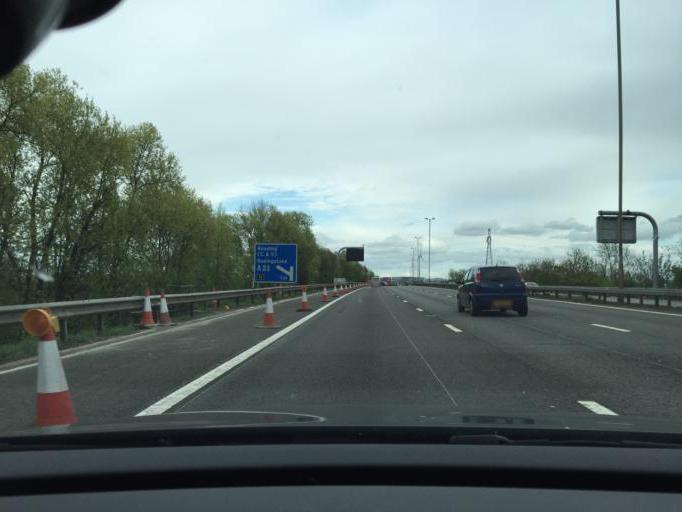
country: GB
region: England
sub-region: West Berkshire
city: Calcot
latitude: 51.4207
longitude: -1.0071
